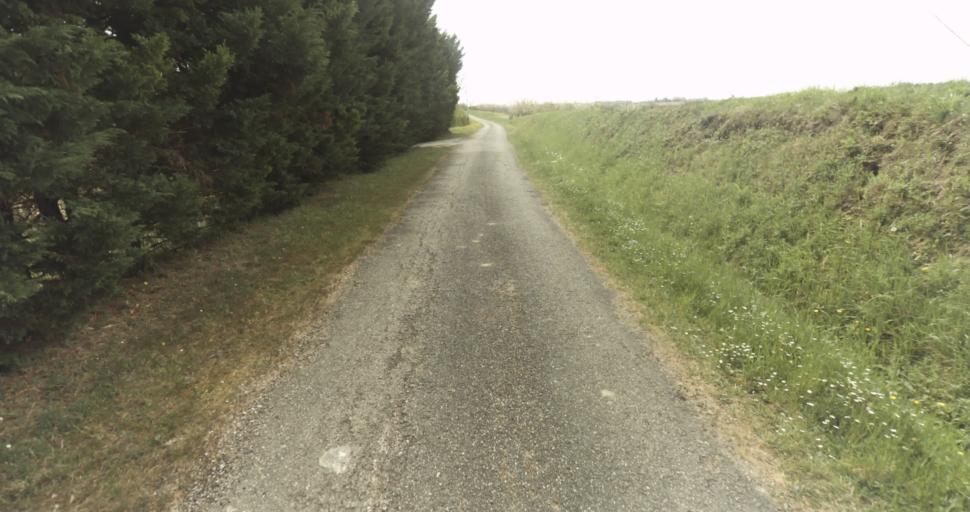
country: FR
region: Midi-Pyrenees
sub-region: Departement du Tarn-et-Garonne
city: Moissac
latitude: 44.1133
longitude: 1.0542
